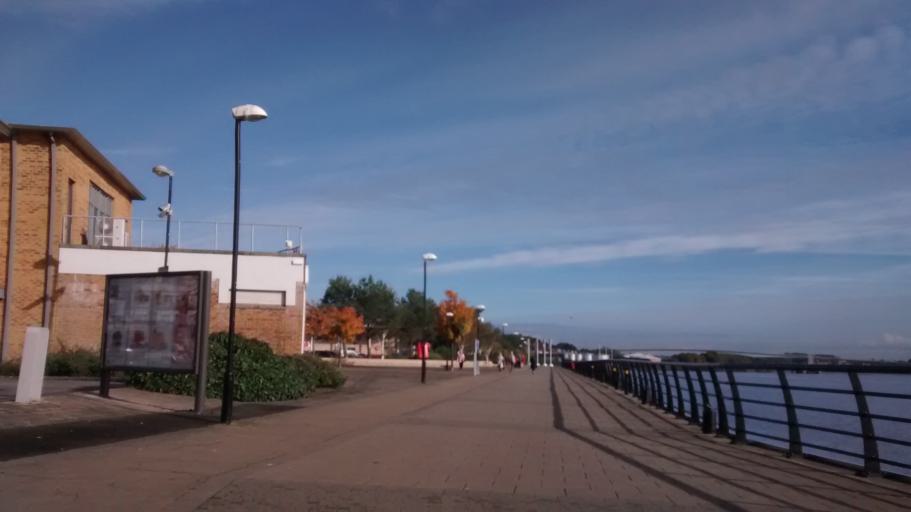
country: GB
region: Northern Ireland
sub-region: City of Derry
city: Derry
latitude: 55.0086
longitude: -7.3168
